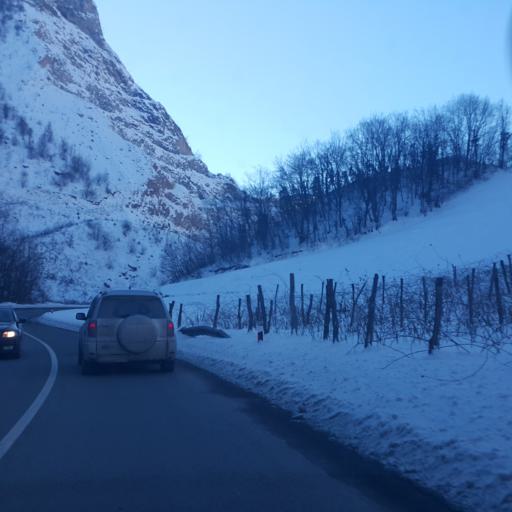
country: RS
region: Central Serbia
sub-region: Rasinski Okrug
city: Aleksandrovac
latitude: 43.3205
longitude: 20.9201
